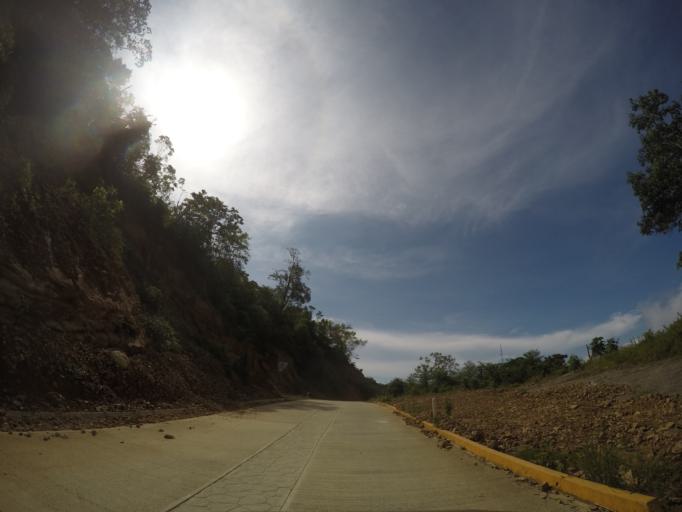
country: MX
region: Oaxaca
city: Pluma Hidalgo
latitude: 15.9306
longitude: -96.4202
